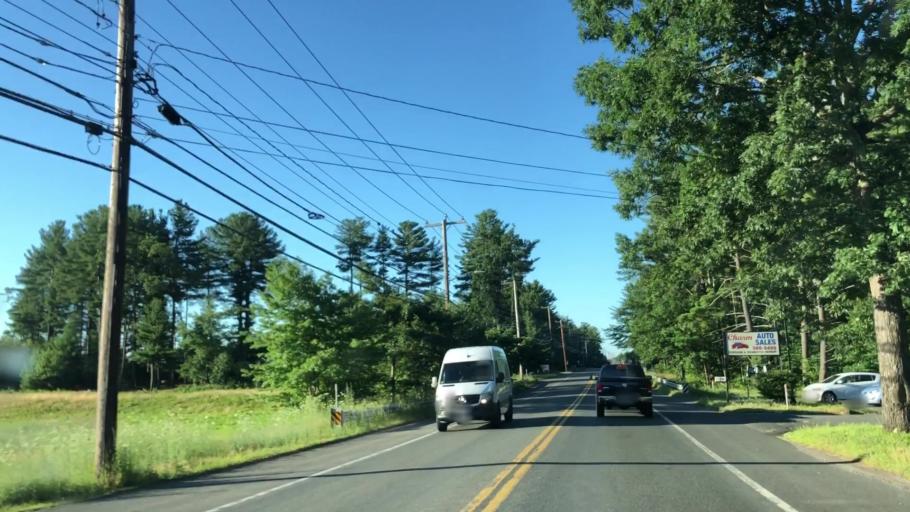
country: US
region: Massachusetts
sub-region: Hampden County
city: Westfield
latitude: 42.1667
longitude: -72.7266
